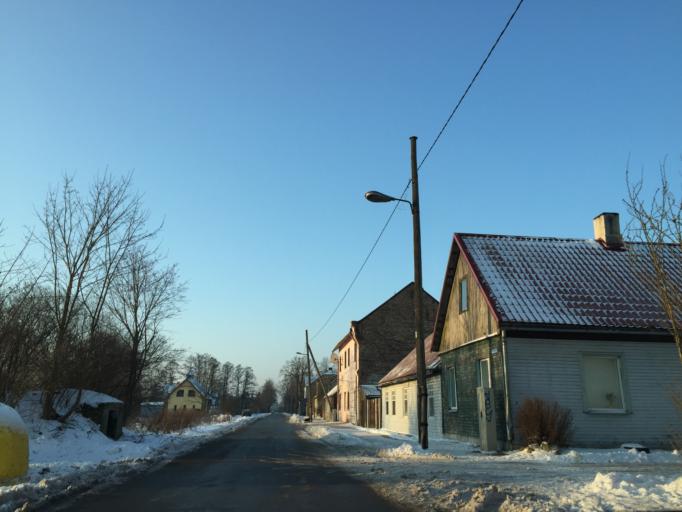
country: LV
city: Tireli
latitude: 56.9412
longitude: 23.6174
